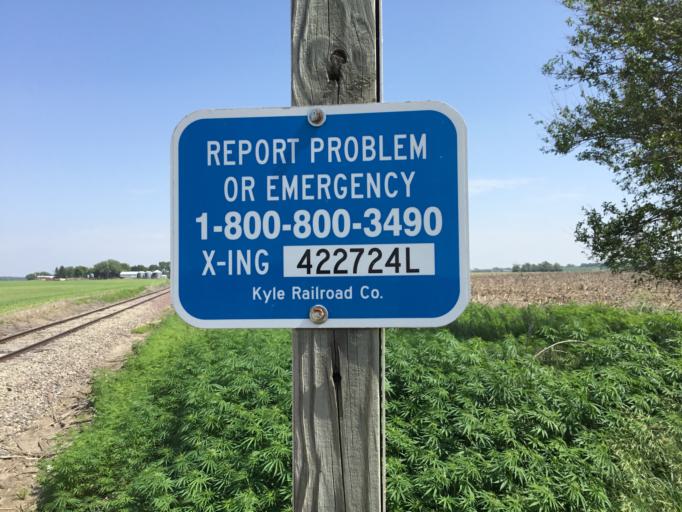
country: US
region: Kansas
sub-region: Republic County
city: Belleville
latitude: 39.7407
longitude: -97.7797
